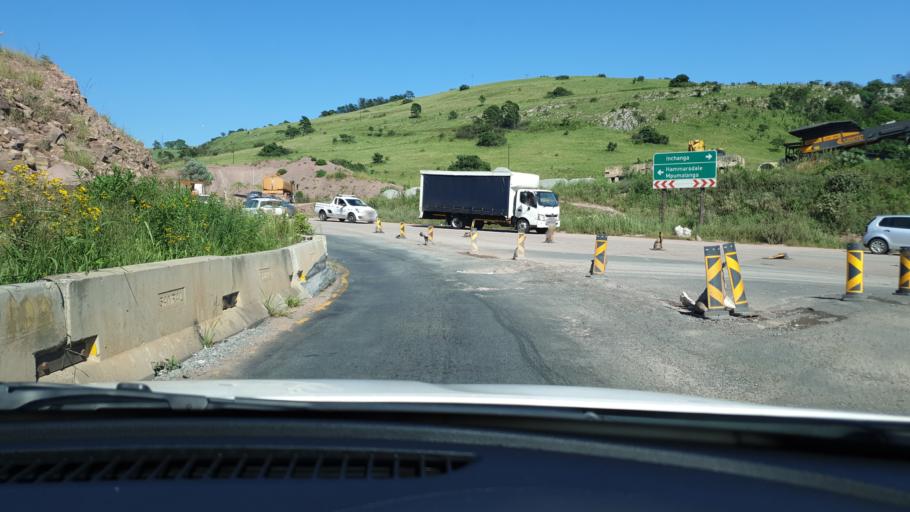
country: ZA
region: KwaZulu-Natal
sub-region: eThekwini Metropolitan Municipality
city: Mpumalanga
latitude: -29.7586
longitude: 30.6657
